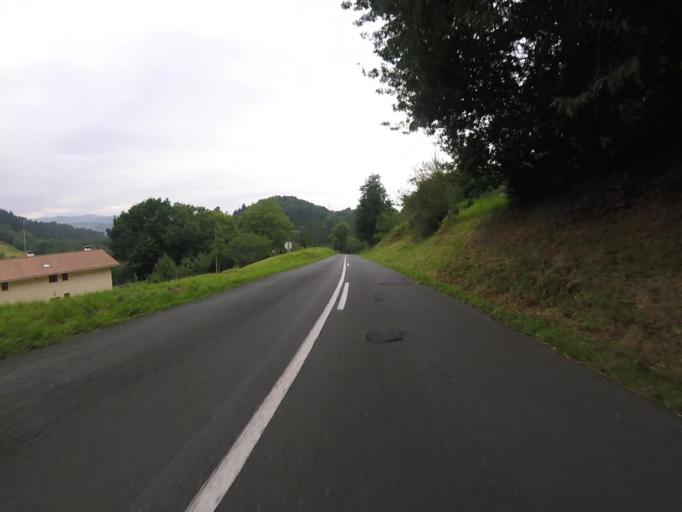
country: ES
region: Basque Country
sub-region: Provincia de Guipuzcoa
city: Lezo
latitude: 43.3116
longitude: -1.8580
